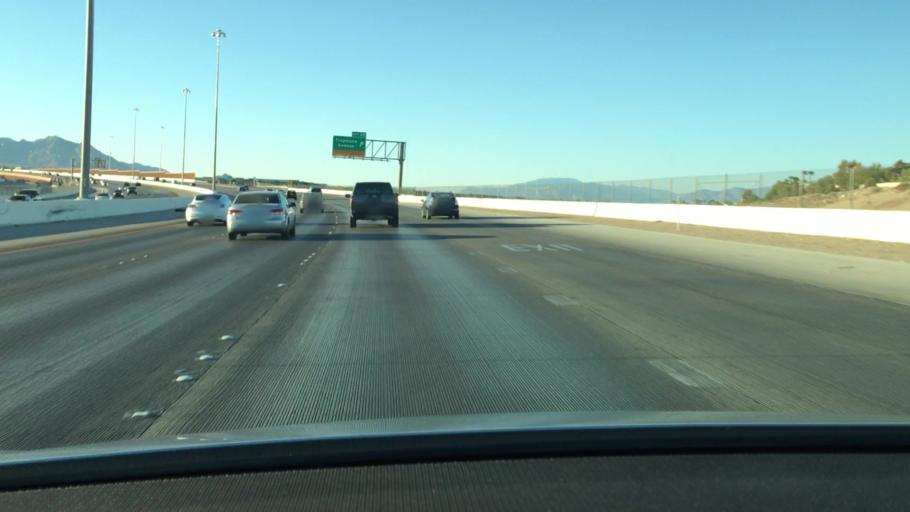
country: US
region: Nevada
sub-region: Clark County
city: Spring Valley
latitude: 36.0927
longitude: -115.2887
